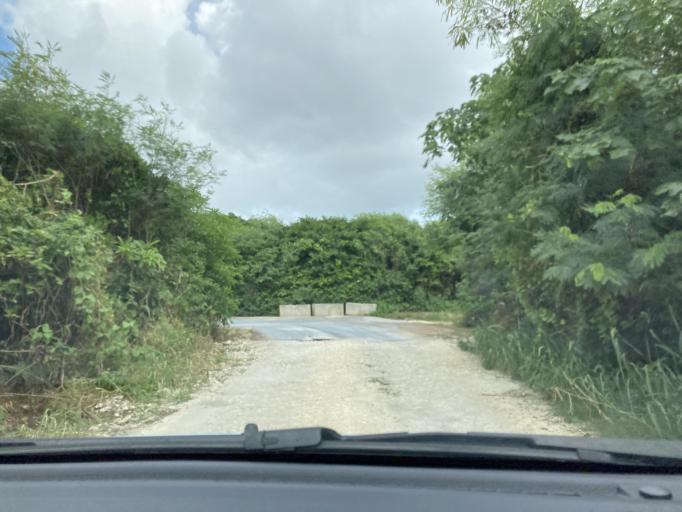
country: JP
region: Okinawa
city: Itoman
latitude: 26.0828
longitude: 127.6872
